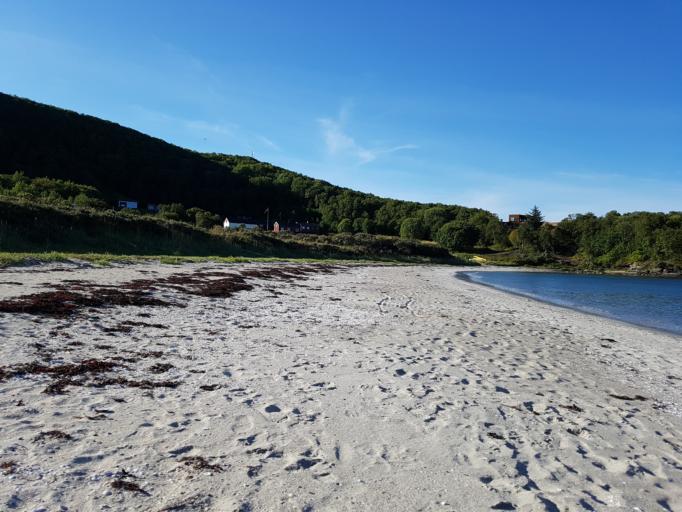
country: NO
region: Sor-Trondelag
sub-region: Afjord
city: A i Afjord
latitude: 64.0517
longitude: 9.9488
